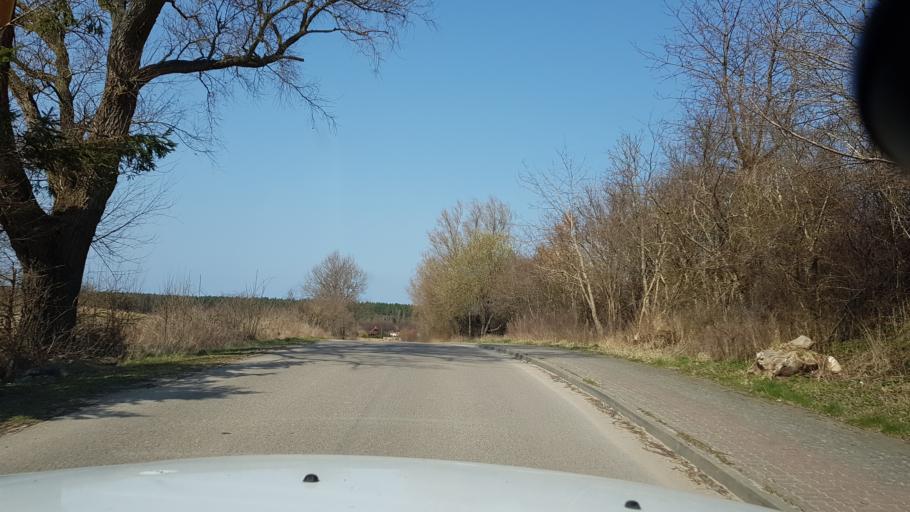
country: PL
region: West Pomeranian Voivodeship
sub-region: Powiat slawienski
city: Darlowo
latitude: 54.5138
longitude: 16.5178
